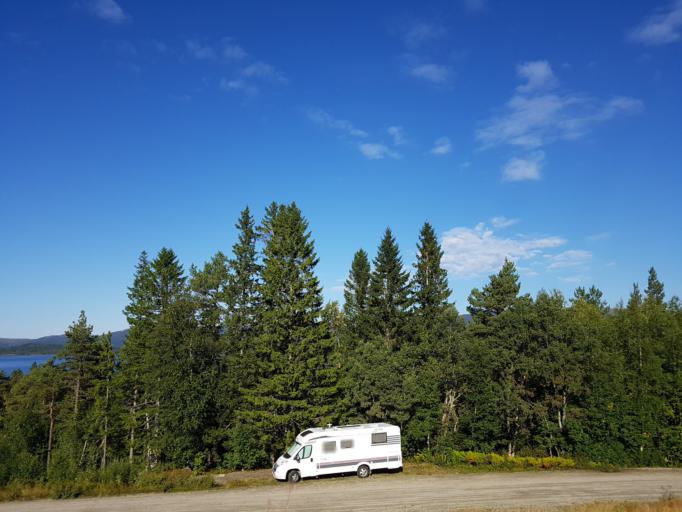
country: NO
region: Sor-Trondelag
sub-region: Trondheim
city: Trondheim
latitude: 63.6273
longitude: 10.2493
